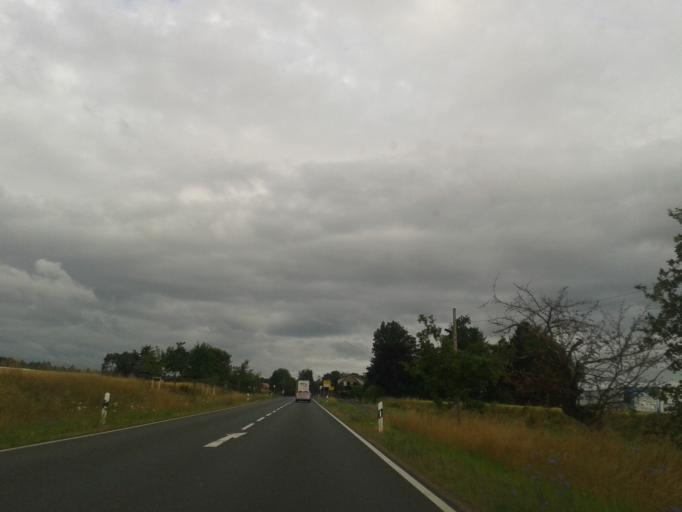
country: DE
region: Saxony
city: Nossen
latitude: 51.0240
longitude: 13.3104
